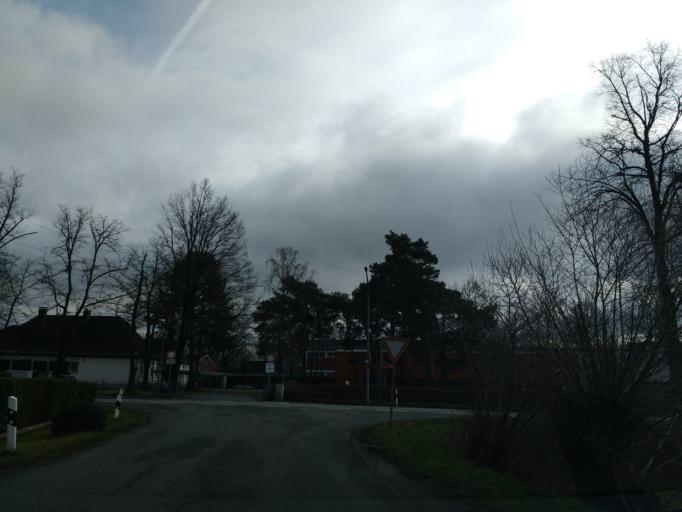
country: DE
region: North Rhine-Westphalia
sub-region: Regierungsbezirk Detmold
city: Hovelhof
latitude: 51.8287
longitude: 8.6835
